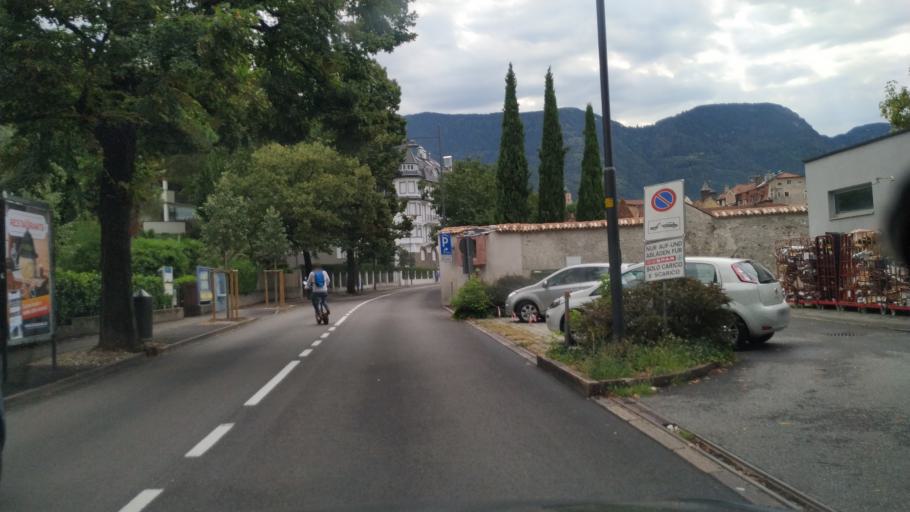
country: IT
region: Trentino-Alto Adige
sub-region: Bolzano
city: Merano
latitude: 46.6748
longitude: 11.1573
